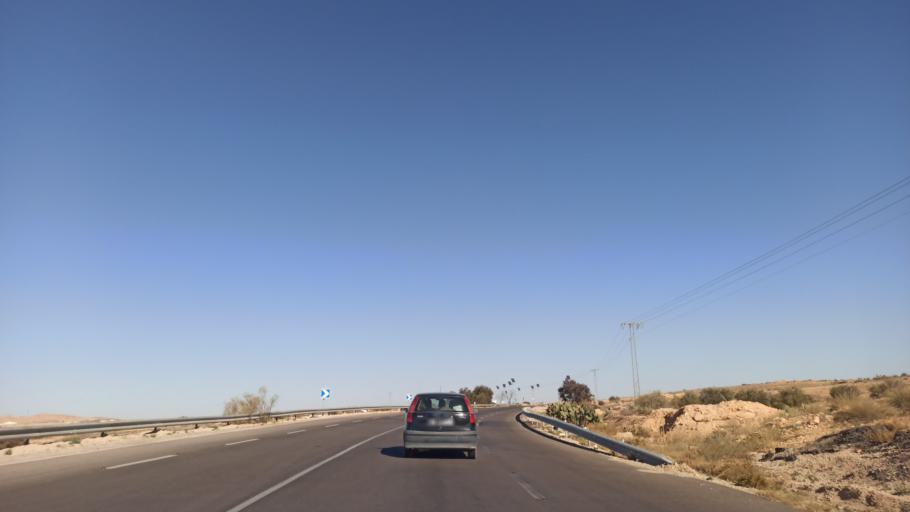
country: TN
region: Sidi Bu Zayd
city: Bi'r al Hufayy
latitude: 34.7237
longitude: 9.0619
